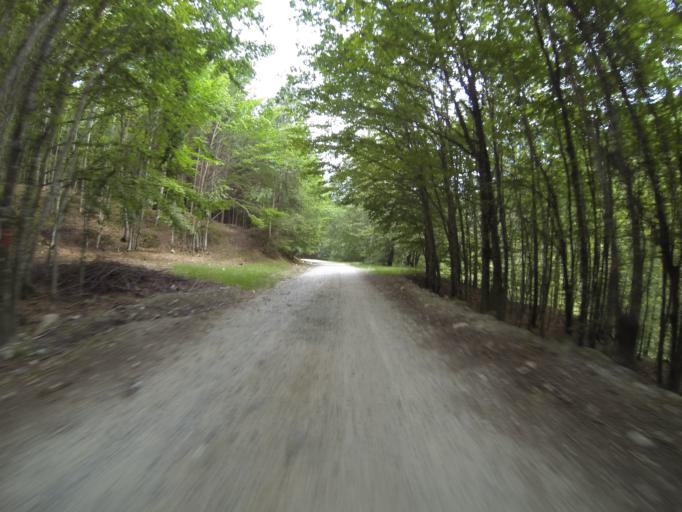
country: RO
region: Gorj
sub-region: Comuna Polovragi
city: Polovragi
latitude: 45.2246
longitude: 23.7715
